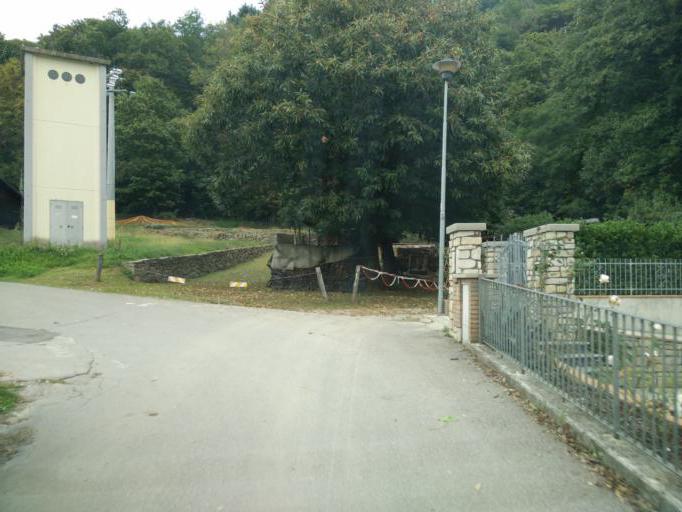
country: IT
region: Tuscany
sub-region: Provincia di Lucca
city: San Romano
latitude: 44.1729
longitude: 10.3422
